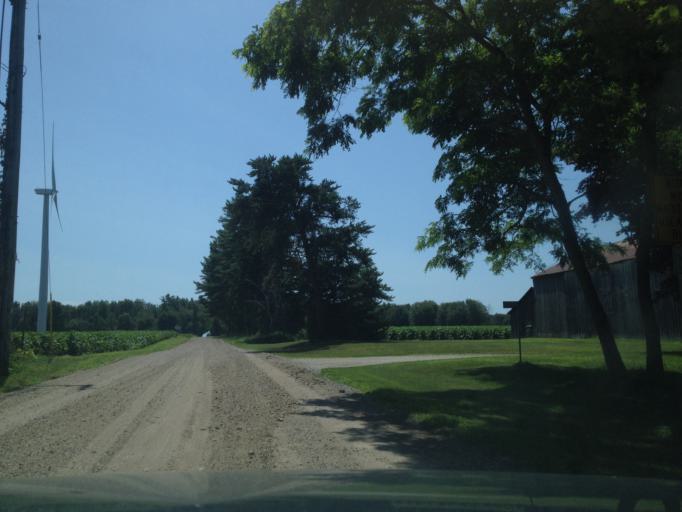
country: CA
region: Ontario
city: Aylmer
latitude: 42.6512
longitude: -80.7704
